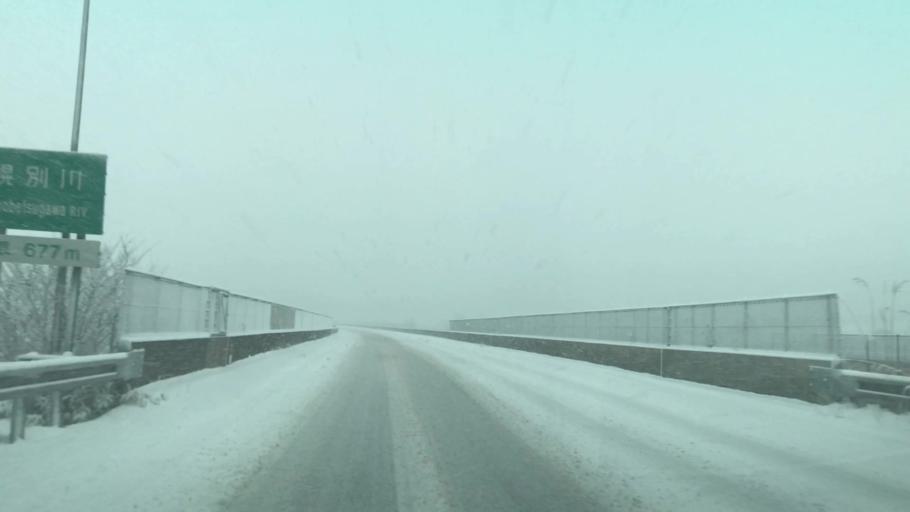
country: JP
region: Hokkaido
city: Muroran
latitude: 42.4206
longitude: 141.0844
